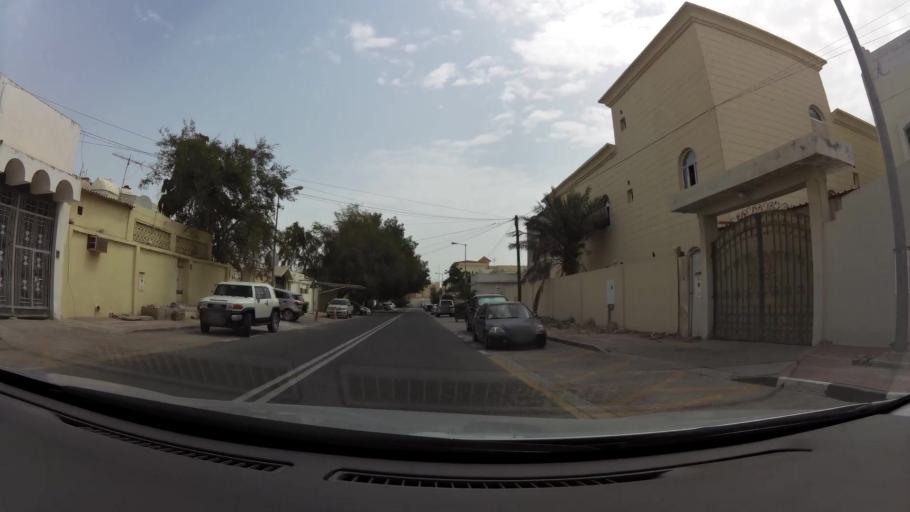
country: QA
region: Baladiyat ad Dawhah
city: Doha
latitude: 25.3117
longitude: 51.4851
